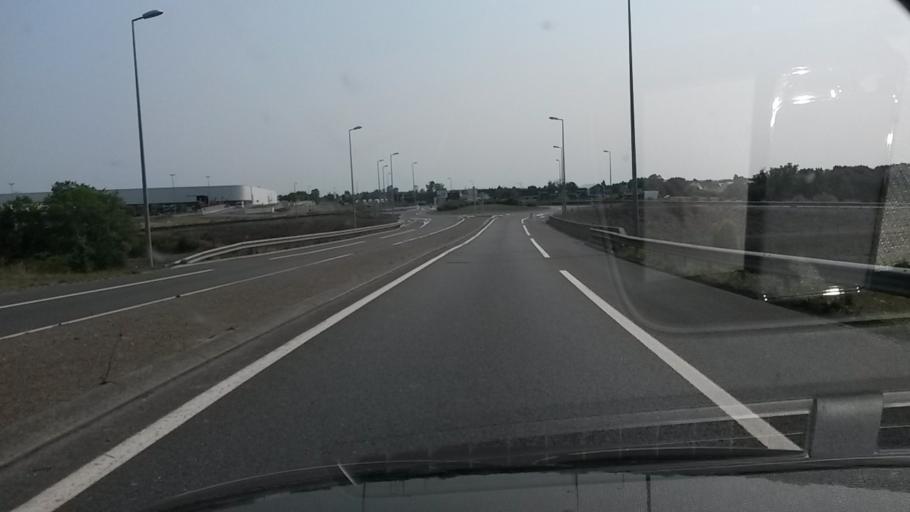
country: FR
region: Pays de la Loire
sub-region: Departement de la Loire-Atlantique
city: Saint-Gereon
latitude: 47.3928
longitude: -1.1890
